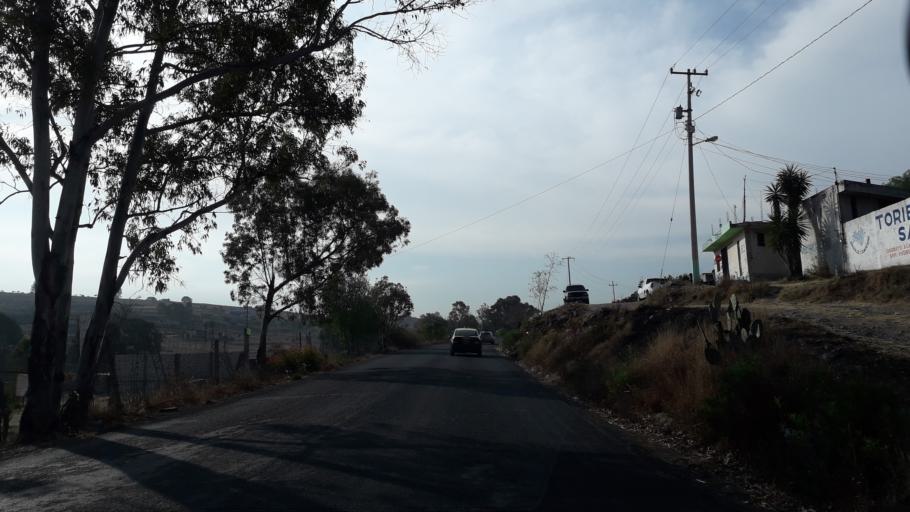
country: MX
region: Puebla
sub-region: Puebla
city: San Andres Azumiatla
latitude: 18.9196
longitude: -98.2492
